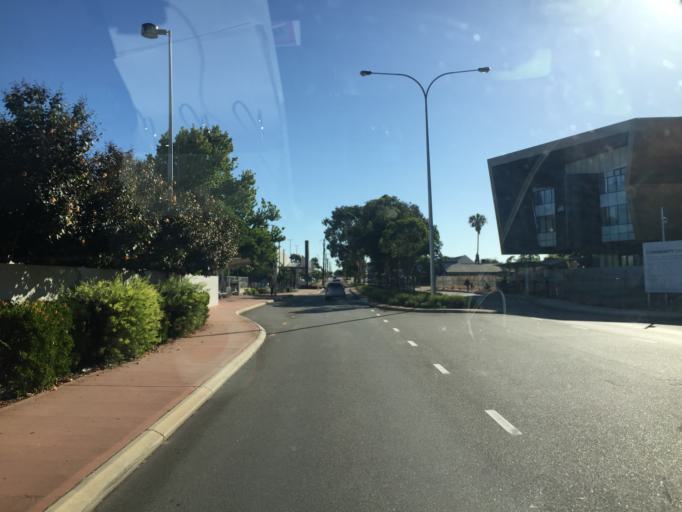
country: AU
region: Western Australia
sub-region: Belmont
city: Belmont
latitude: -31.9630
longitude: 115.9351
